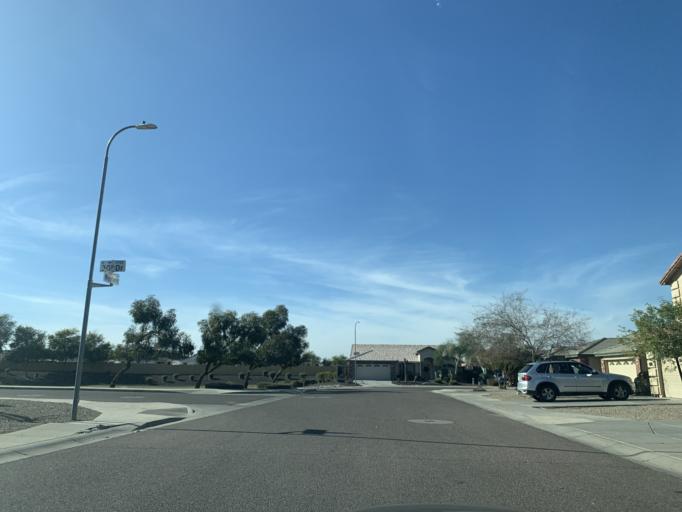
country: US
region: Arizona
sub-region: Maricopa County
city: Laveen
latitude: 33.3943
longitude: -112.1228
